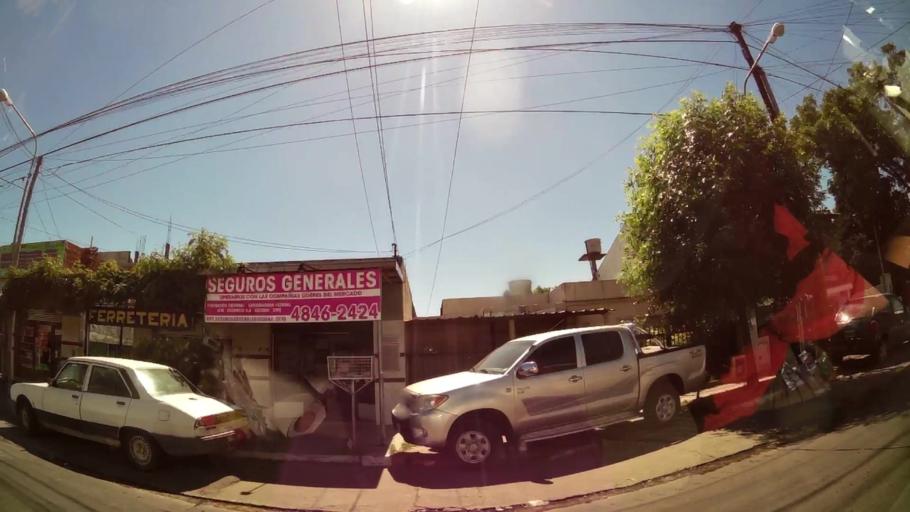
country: AR
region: Buenos Aires
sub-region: Partido de Tigre
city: Tigre
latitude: -34.4965
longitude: -58.6156
